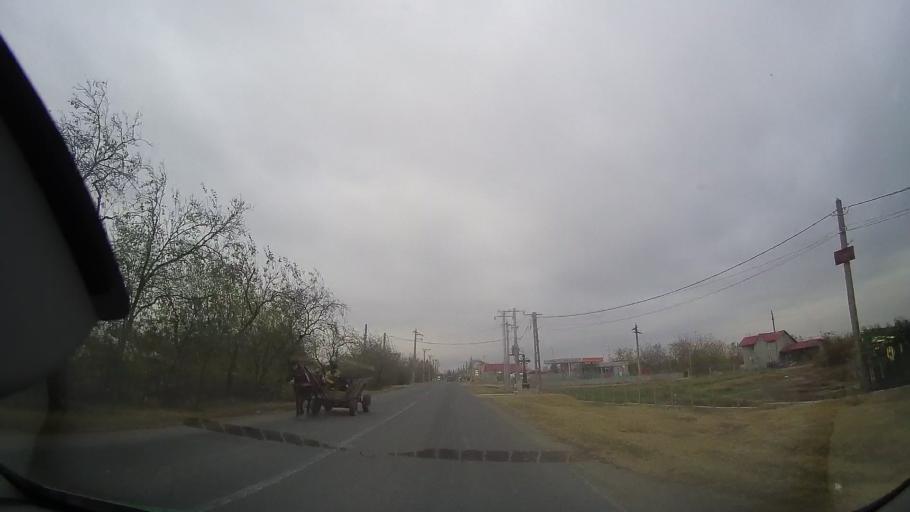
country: RO
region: Buzau
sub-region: Comuna Padina
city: Padina
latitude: 44.8209
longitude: 27.1182
